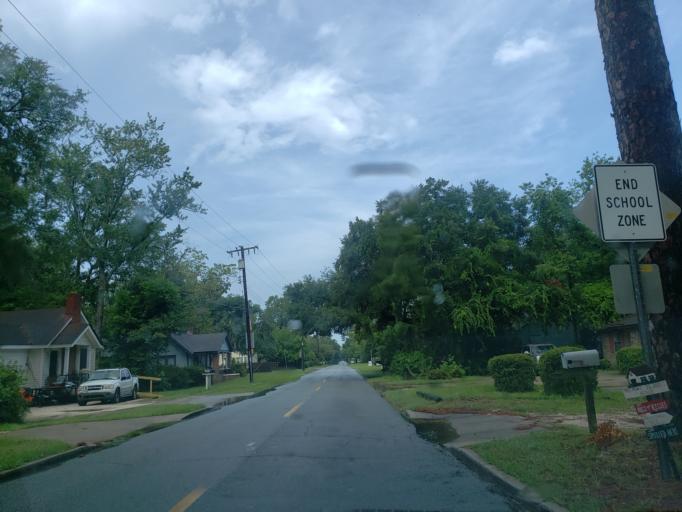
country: US
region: Georgia
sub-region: Chatham County
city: Thunderbolt
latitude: 32.0323
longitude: -81.0740
